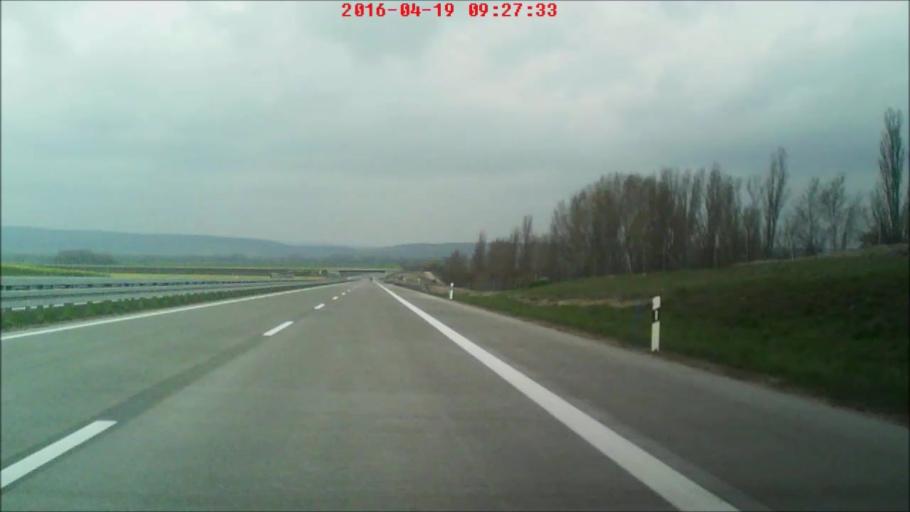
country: DE
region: Thuringia
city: Schillingstedt
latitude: 51.2189
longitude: 11.1853
